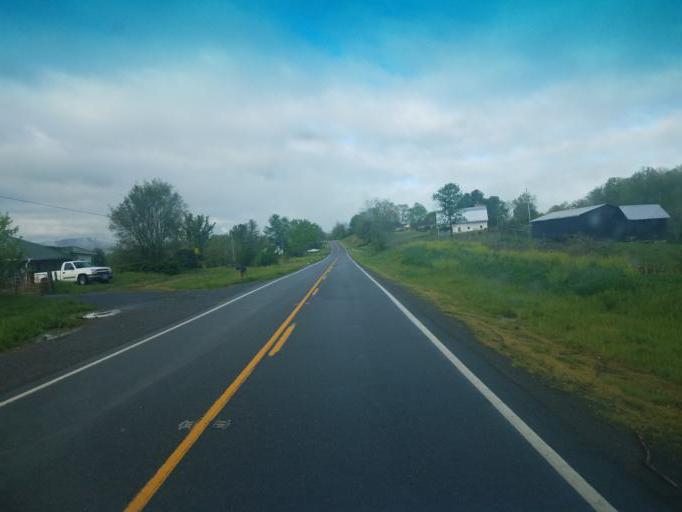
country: US
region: Virginia
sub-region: Washington County
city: Emory
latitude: 36.7051
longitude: -81.7858
